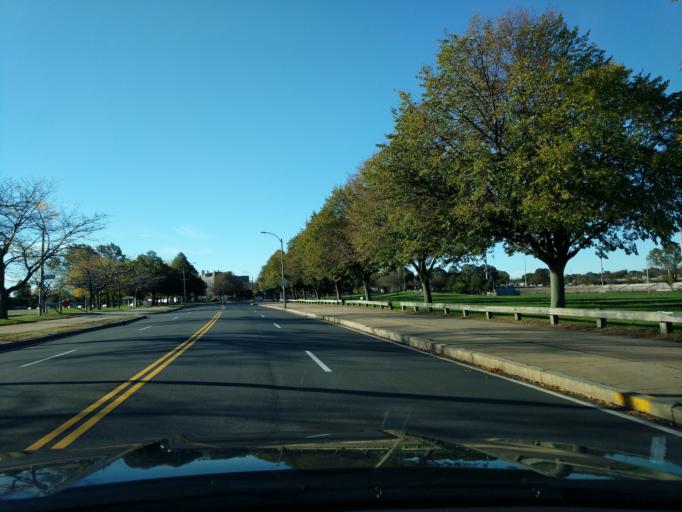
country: US
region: Massachusetts
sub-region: Suffolk County
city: South Boston
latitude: 42.3253
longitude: -71.0489
